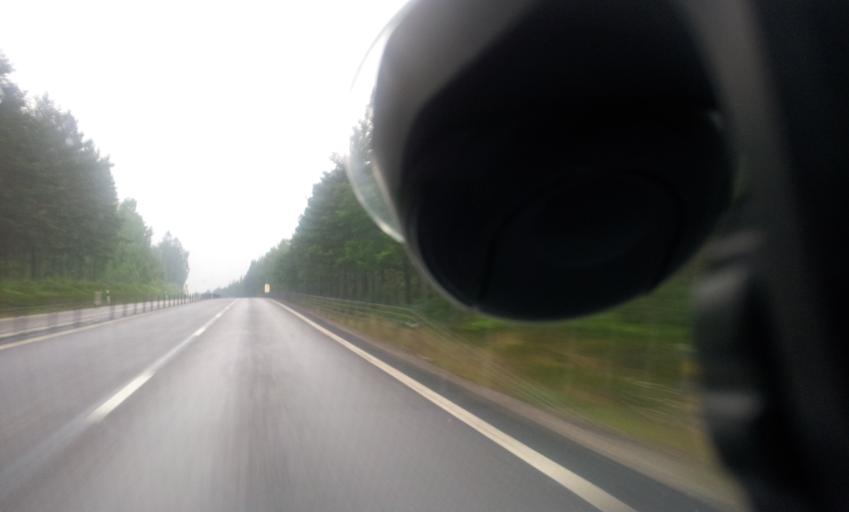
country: SE
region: Kalmar
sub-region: Vasterviks Kommun
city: Gamleby
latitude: 57.8232
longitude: 16.4622
